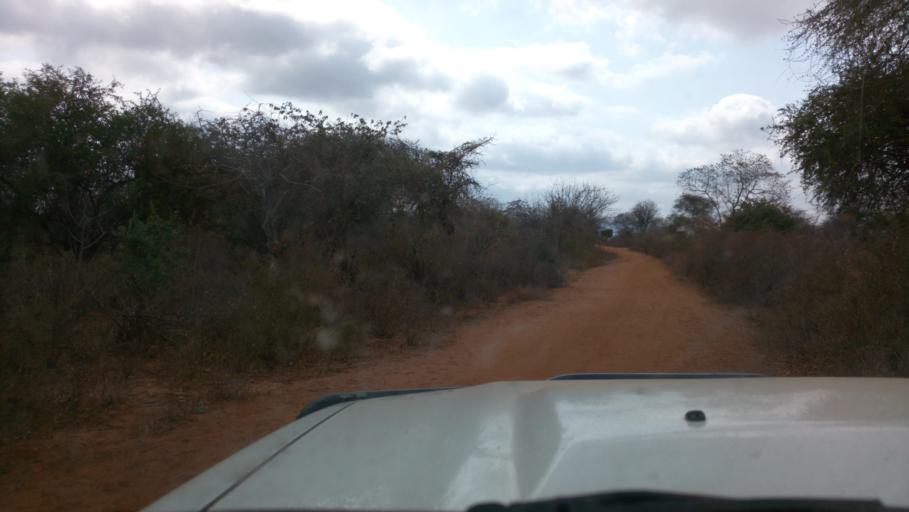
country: KE
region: Kitui
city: Kitui
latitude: -1.8318
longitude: 38.3185
